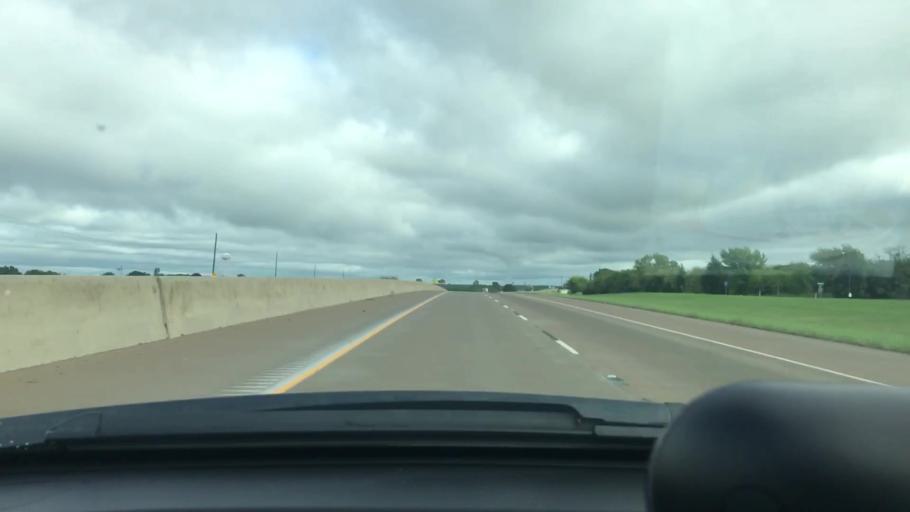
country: US
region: Texas
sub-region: Grayson County
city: Howe
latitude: 33.4934
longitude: -96.6199
